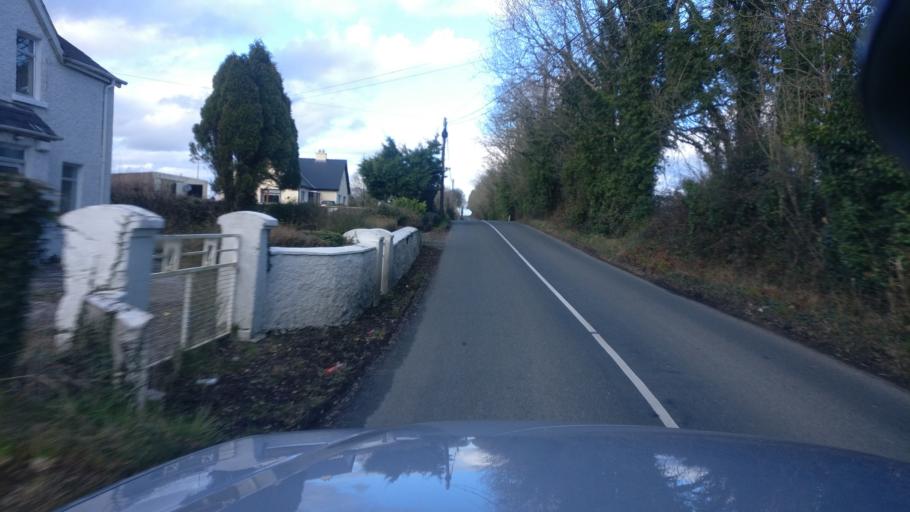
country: IE
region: Connaught
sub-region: County Galway
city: Loughrea
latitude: 53.2161
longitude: -8.3965
